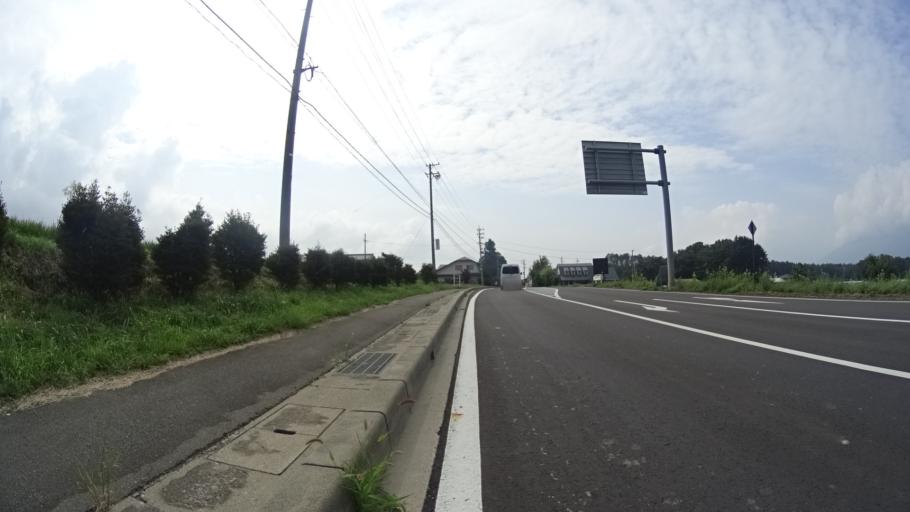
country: JP
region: Nagano
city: Chino
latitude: 35.9465
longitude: 138.2426
